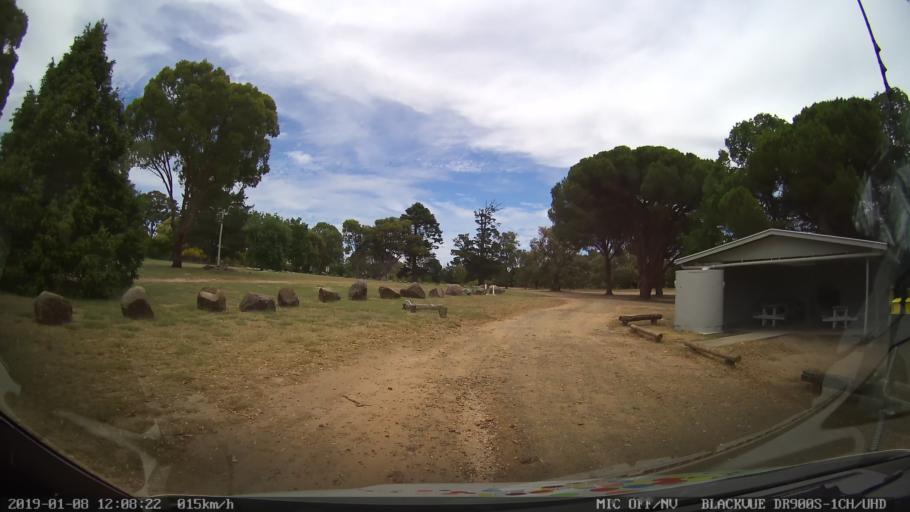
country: AU
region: New South Wales
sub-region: Armidale Dumaresq
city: Armidale
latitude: -30.4298
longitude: 151.5972
